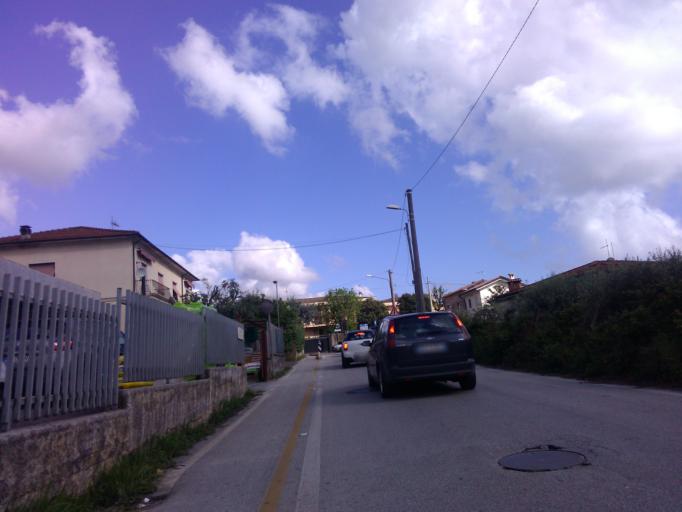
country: IT
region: Tuscany
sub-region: Provincia di Massa-Carrara
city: Massa
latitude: 44.0216
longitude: 10.1234
